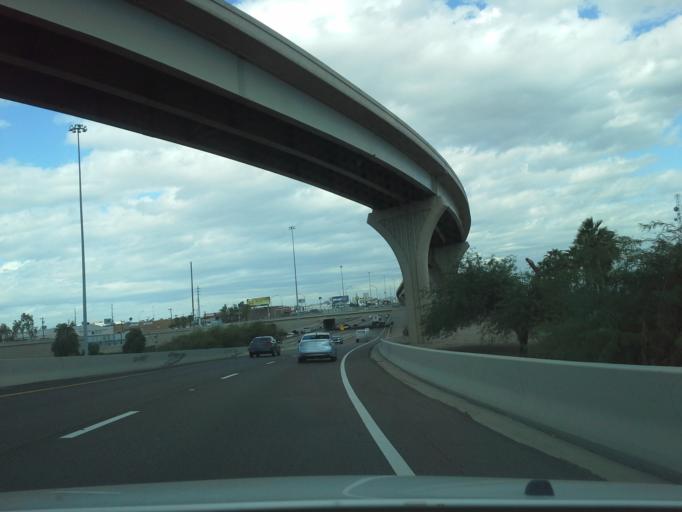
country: US
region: Arizona
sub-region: Maricopa County
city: Phoenix
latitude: 33.4635
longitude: -112.1083
